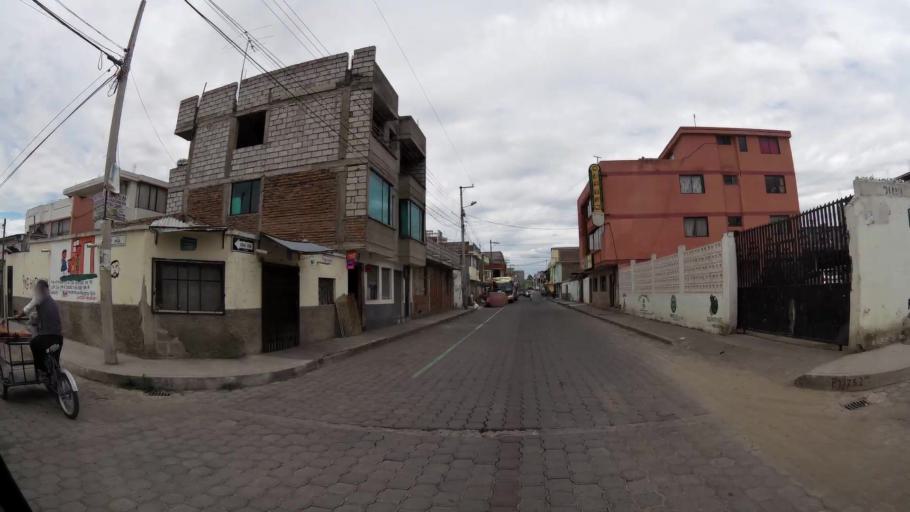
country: EC
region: Cotopaxi
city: San Miguel de Salcedo
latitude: -1.0461
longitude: -78.5869
